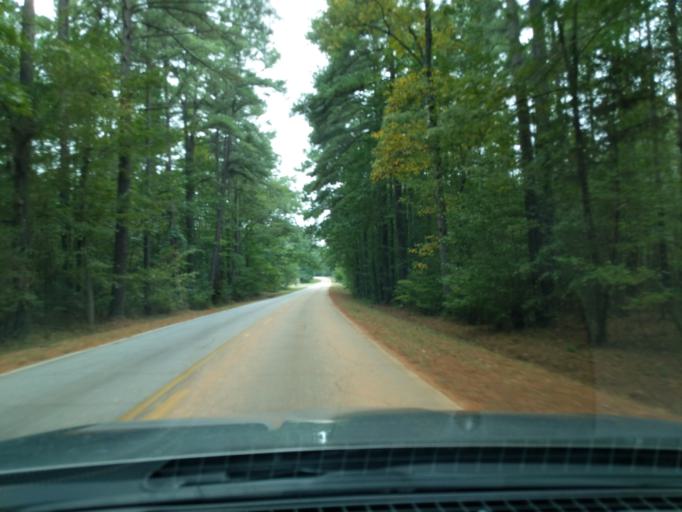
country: US
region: Georgia
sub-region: Columbia County
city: Appling
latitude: 33.6373
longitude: -82.3929
